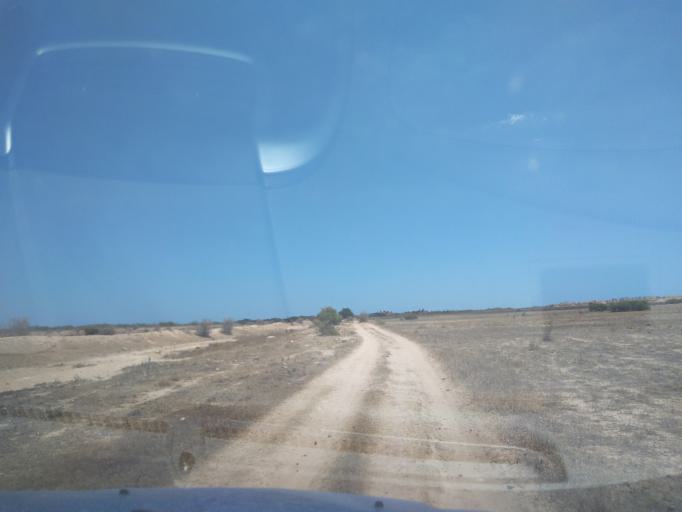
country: TN
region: Susah
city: Harqalah
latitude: 36.1721
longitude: 10.4384
